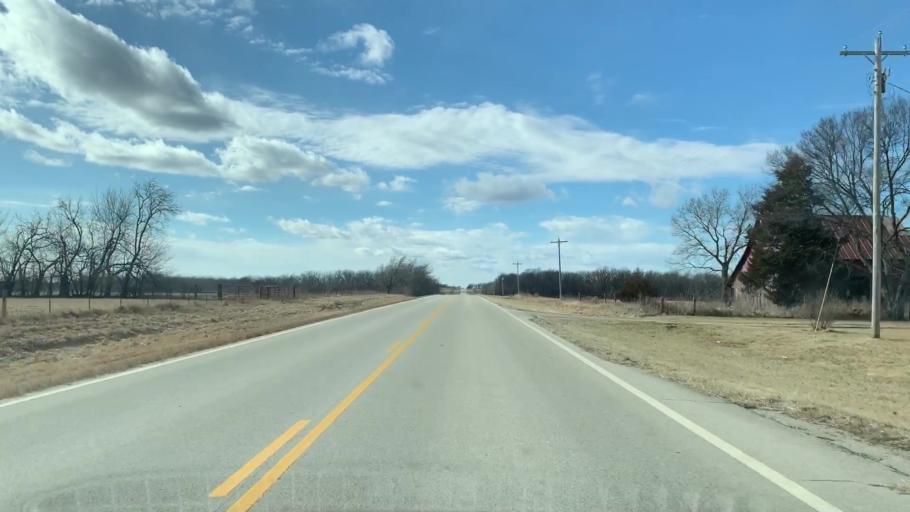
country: US
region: Kansas
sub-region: Neosho County
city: Chanute
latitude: 37.5290
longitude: -95.4197
